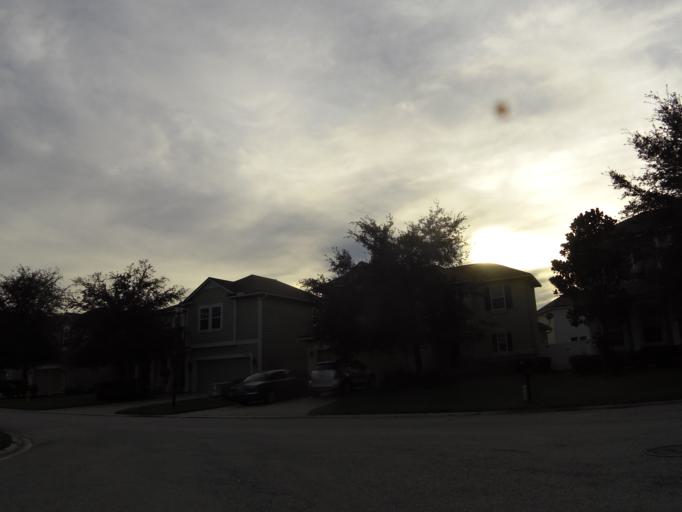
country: US
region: Florida
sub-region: Saint Johns County
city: Fruit Cove
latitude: 30.1529
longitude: -81.5316
